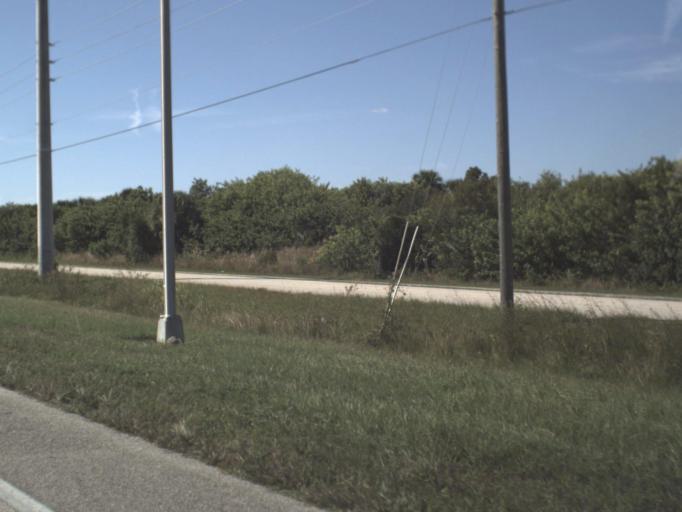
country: US
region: Florida
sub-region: Charlotte County
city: Rotonda
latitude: 26.9329
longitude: -82.2373
